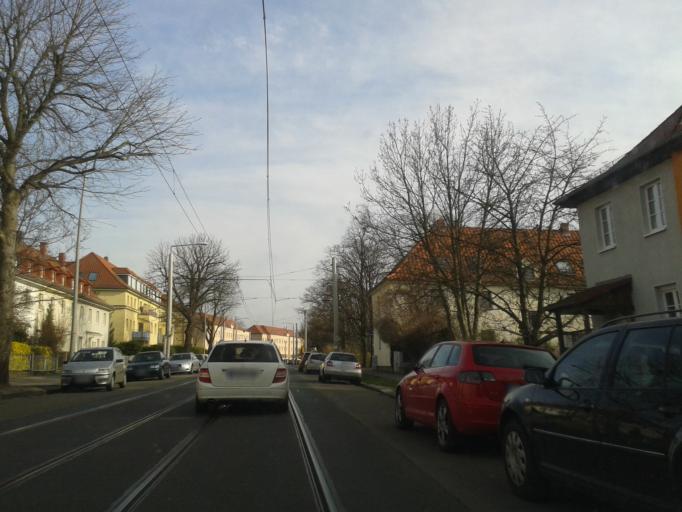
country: DE
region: Saxony
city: Dresden
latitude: 51.0233
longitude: 13.7639
